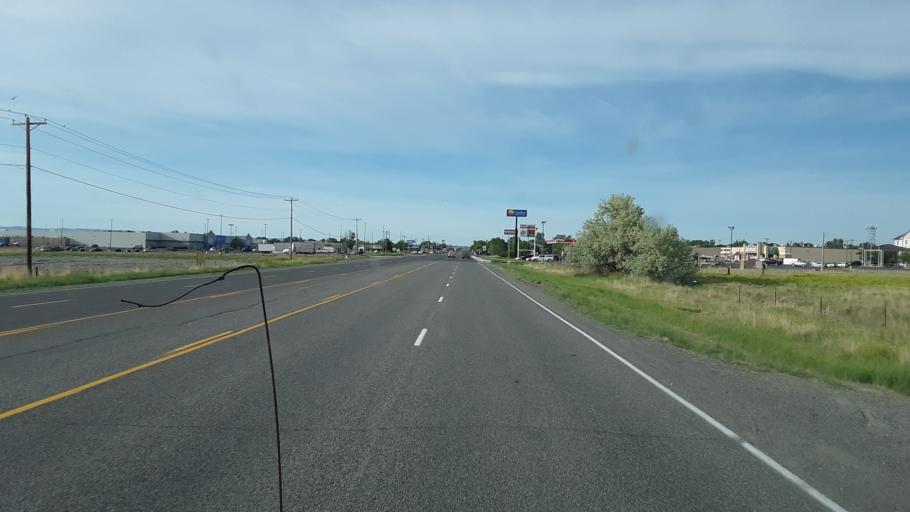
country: US
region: Wyoming
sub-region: Fremont County
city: Riverton
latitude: 43.0469
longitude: -108.3808
